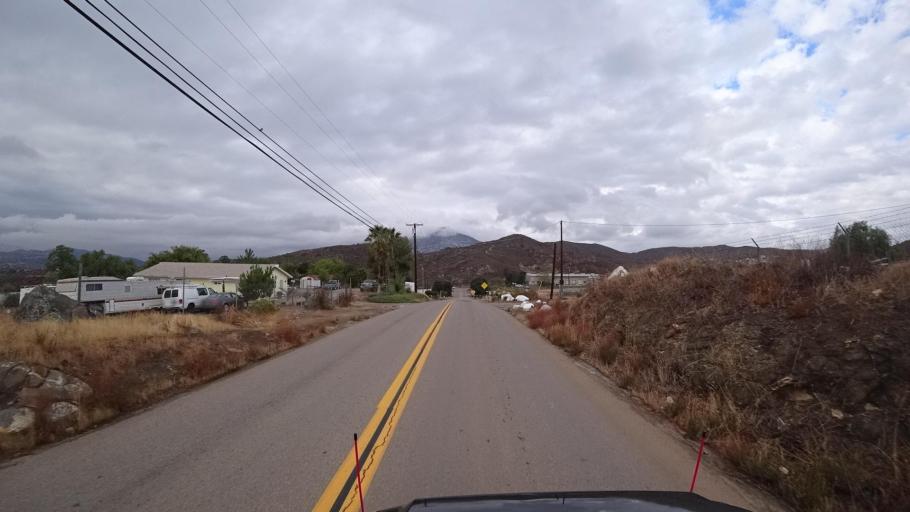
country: MX
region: Baja California
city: Tecate
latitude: 32.5827
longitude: -116.6300
